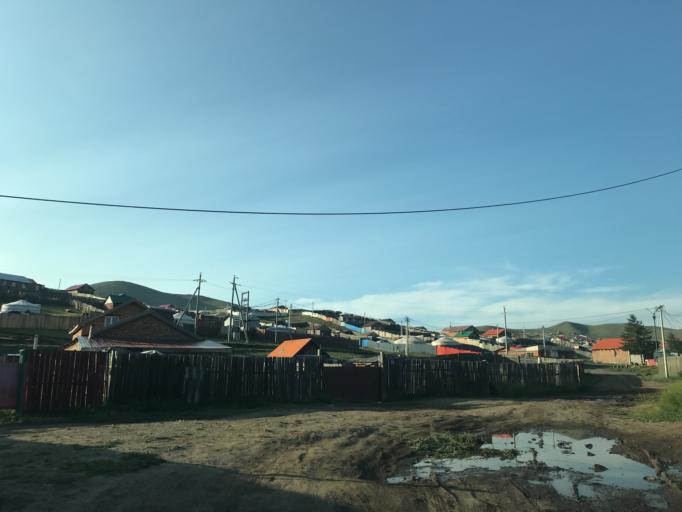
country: MN
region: Ulaanbaatar
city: Ulaanbaatar
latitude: 47.9884
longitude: 106.9621
